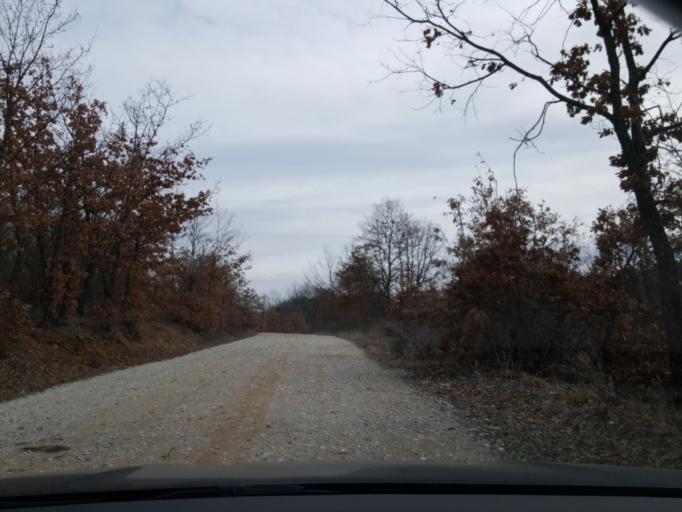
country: RS
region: Central Serbia
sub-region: Pirotski Okrug
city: Dimitrovgrad
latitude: 43.0022
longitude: 22.7492
